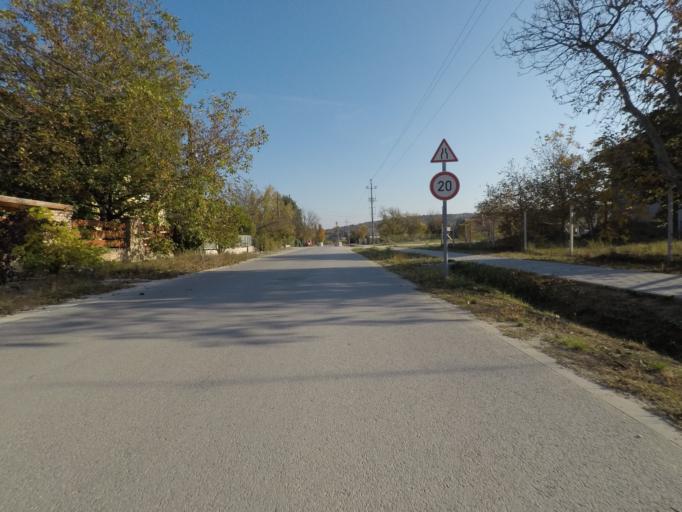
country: HU
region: Pest
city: Budakalasz
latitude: 47.6253
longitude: 19.0402
